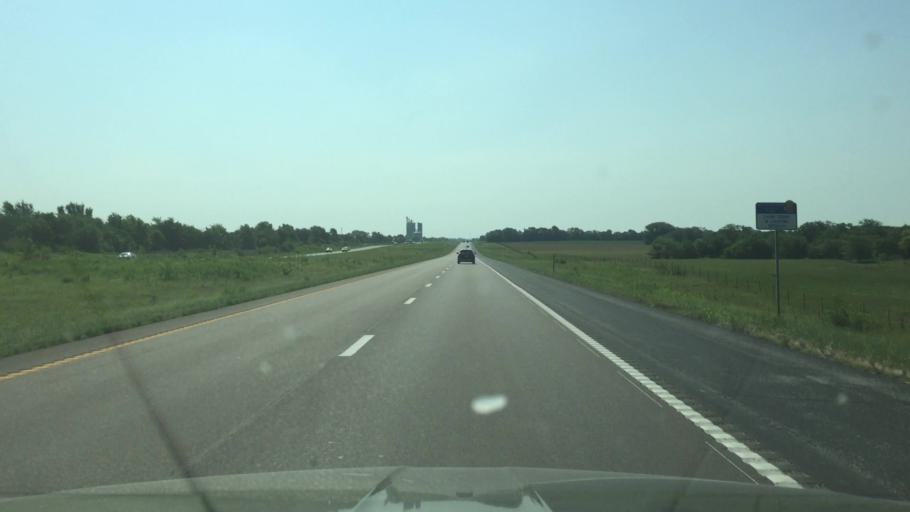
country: US
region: Missouri
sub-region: Pettis County
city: La Monte
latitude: 38.7590
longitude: -93.3710
